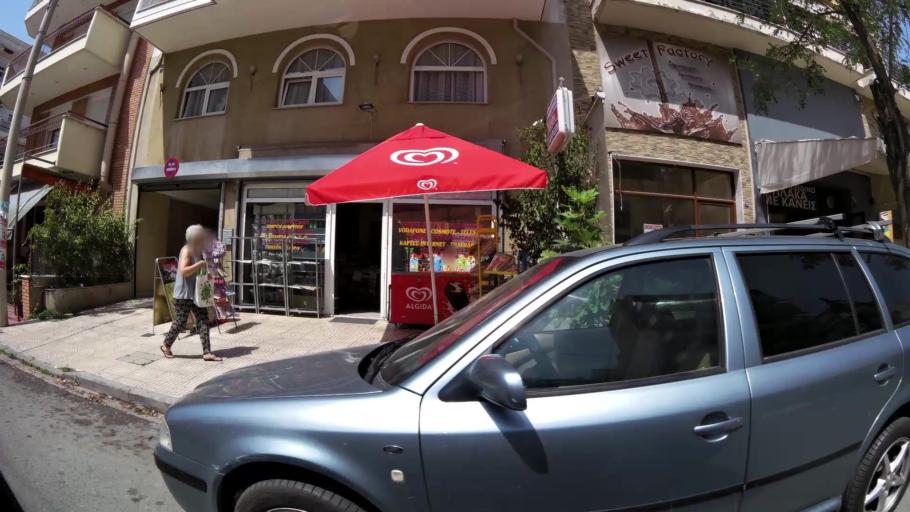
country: GR
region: Central Macedonia
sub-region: Nomos Thessalonikis
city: Evosmos
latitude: 40.6715
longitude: 22.9156
